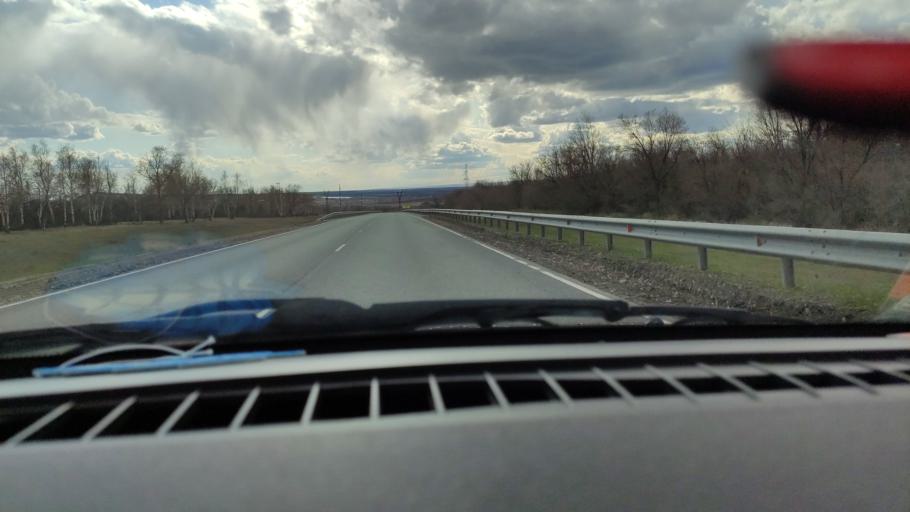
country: RU
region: Saratov
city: Tersa
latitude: 52.0840
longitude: 47.6742
